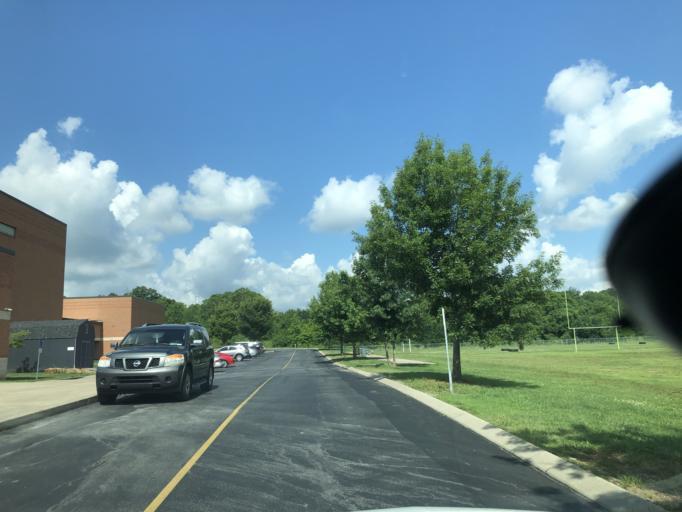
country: US
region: Tennessee
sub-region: Rutherford County
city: La Vergne
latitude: 36.0318
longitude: -86.6209
